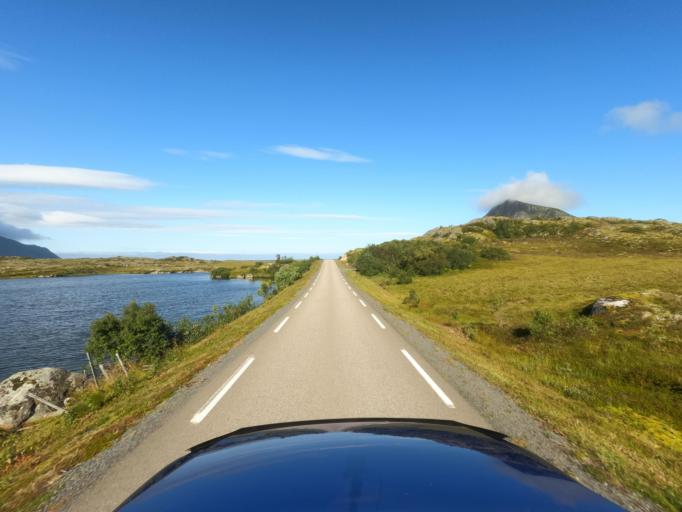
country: NO
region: Nordland
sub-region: Vestvagoy
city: Evjen
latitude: 68.3104
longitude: 14.0962
